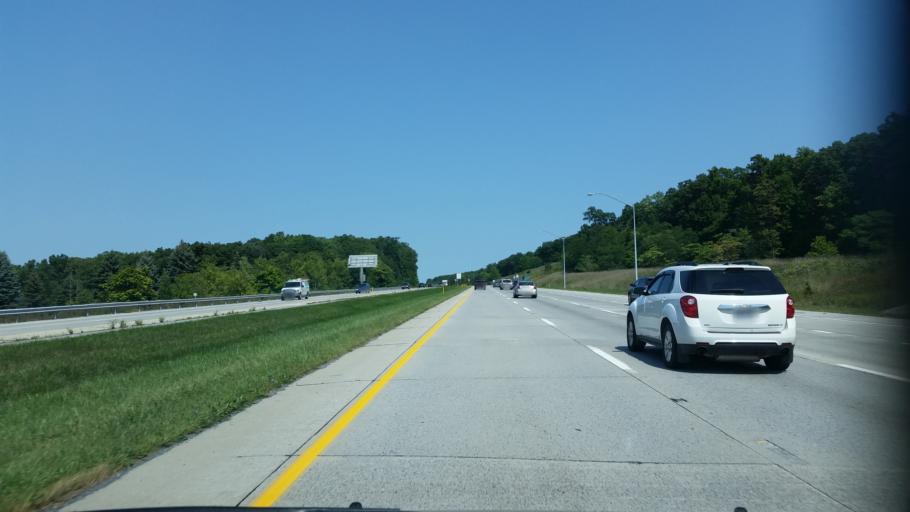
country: US
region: Pennsylvania
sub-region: Blair County
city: Altoona
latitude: 40.4996
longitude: -78.3776
